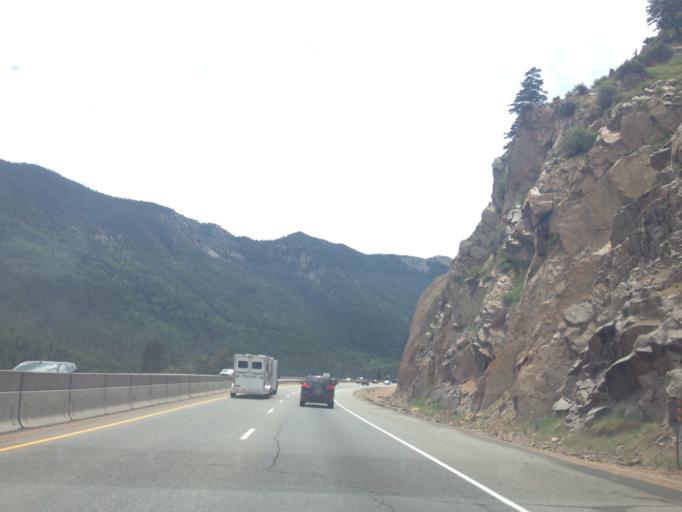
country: US
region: Colorado
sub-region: Clear Creek County
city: Georgetown
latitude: 39.7017
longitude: -105.7078
